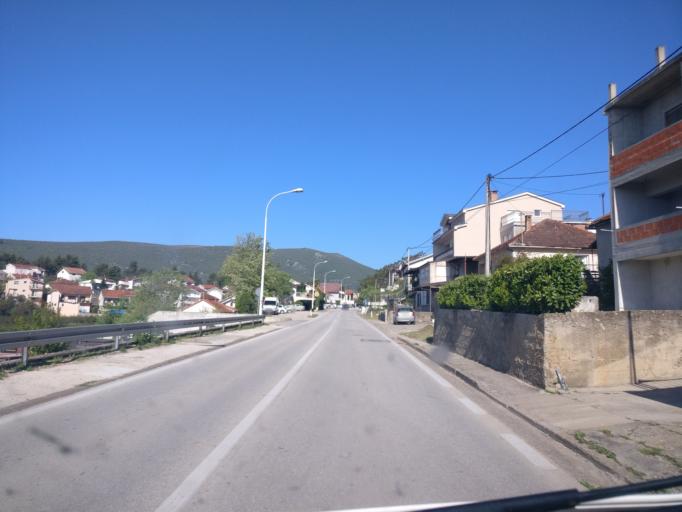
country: BA
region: Federation of Bosnia and Herzegovina
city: Capljina
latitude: 43.1189
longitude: 17.6907
